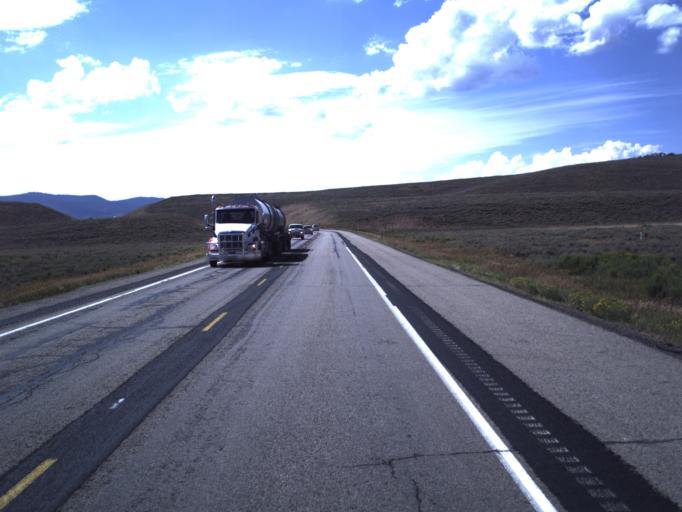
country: US
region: Utah
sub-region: Wasatch County
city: Heber
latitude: 40.2292
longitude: -111.1186
